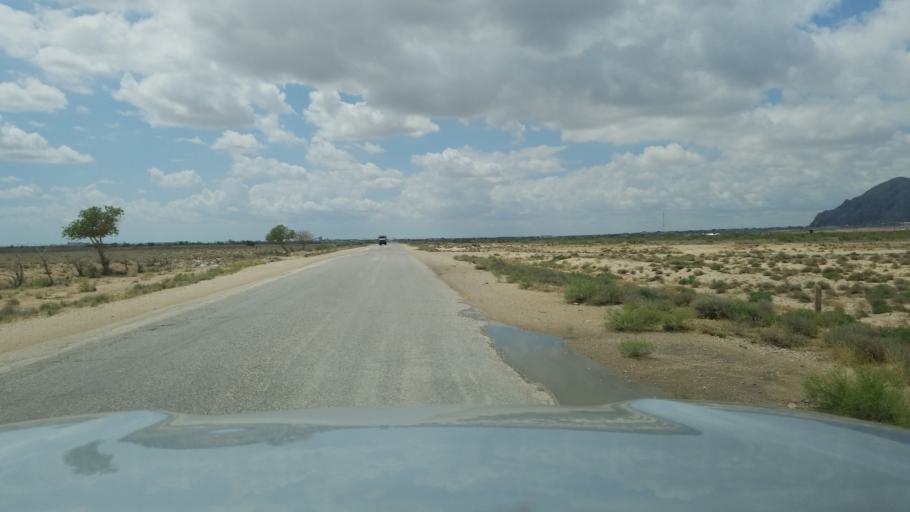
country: TM
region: Balkan
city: Balkanabat
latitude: 39.4853
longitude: 54.4256
